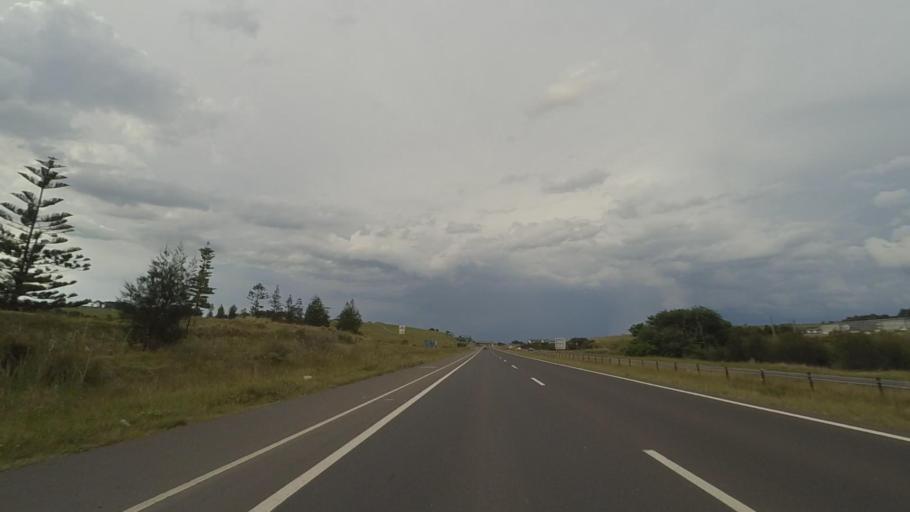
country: AU
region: New South Wales
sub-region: Shellharbour
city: Croom
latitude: -34.5966
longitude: 150.8421
